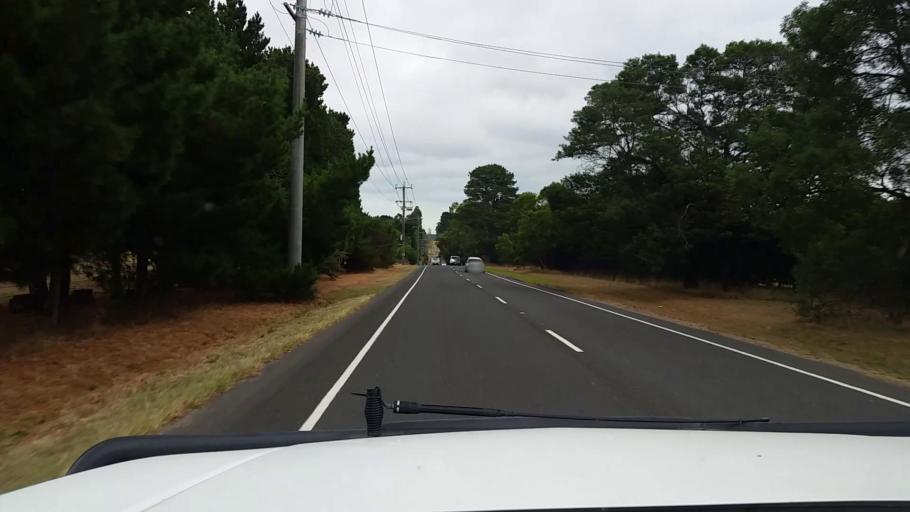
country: AU
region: Victoria
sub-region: Mornington Peninsula
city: Moorooduc
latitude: -38.2821
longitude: 145.1186
